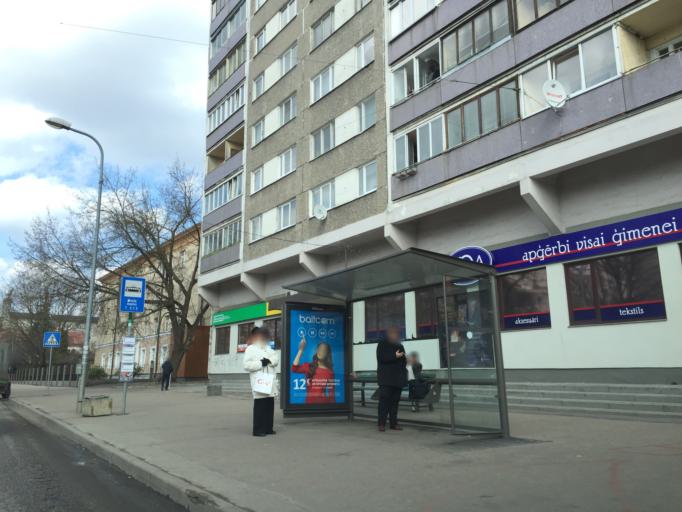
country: LV
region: Riga
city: Riga
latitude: 56.9254
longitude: 24.1683
